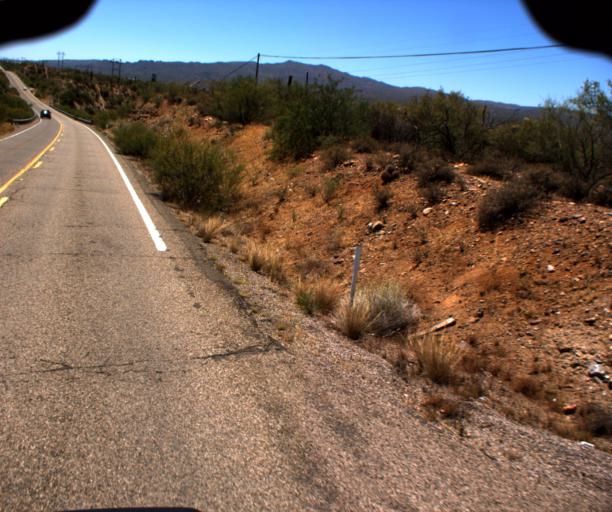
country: US
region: Arizona
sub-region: Pinal County
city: Kearny
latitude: 33.0762
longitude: -110.9225
